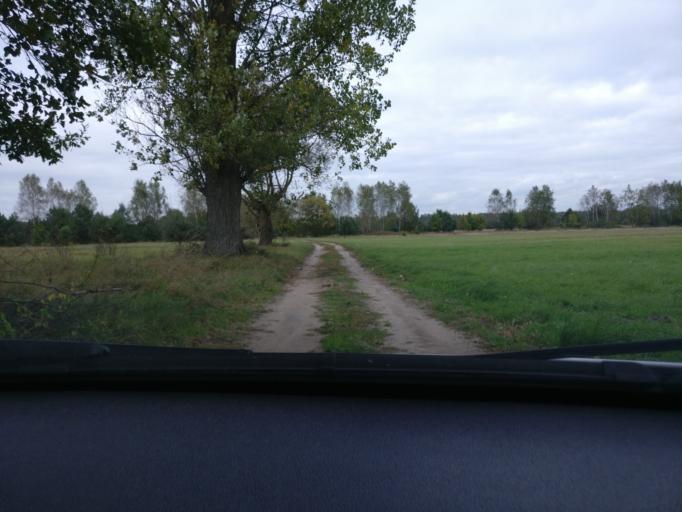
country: PL
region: Masovian Voivodeship
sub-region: Powiat kozienicki
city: Garbatka-Letnisko
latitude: 51.5176
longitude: 21.5991
